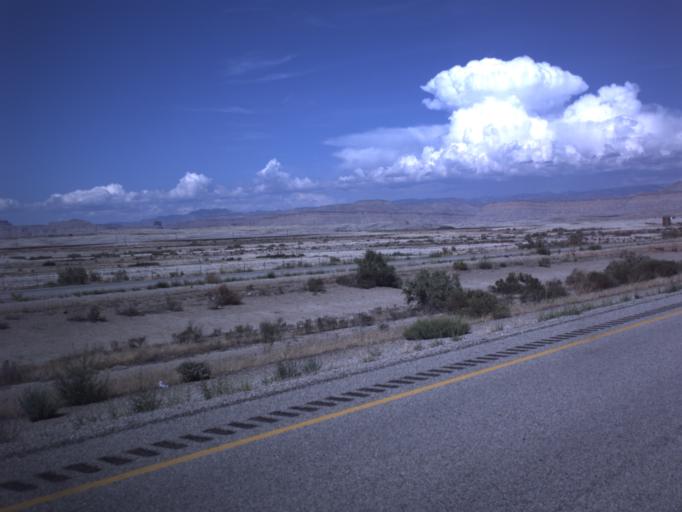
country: US
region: Utah
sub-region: Carbon County
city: East Carbon City
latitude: 38.9877
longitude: -110.2039
